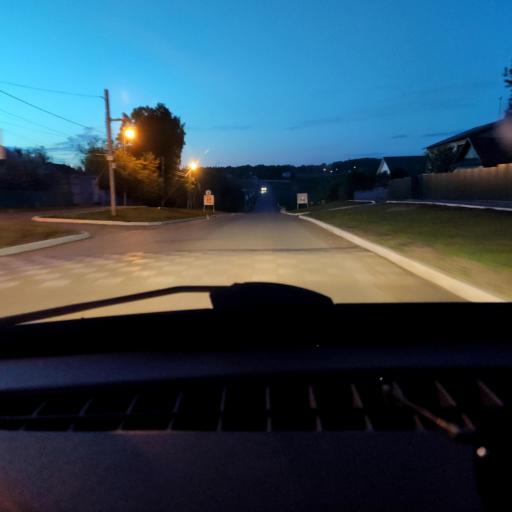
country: RU
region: Bashkortostan
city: Karmaskaly
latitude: 54.3723
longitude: 56.1726
